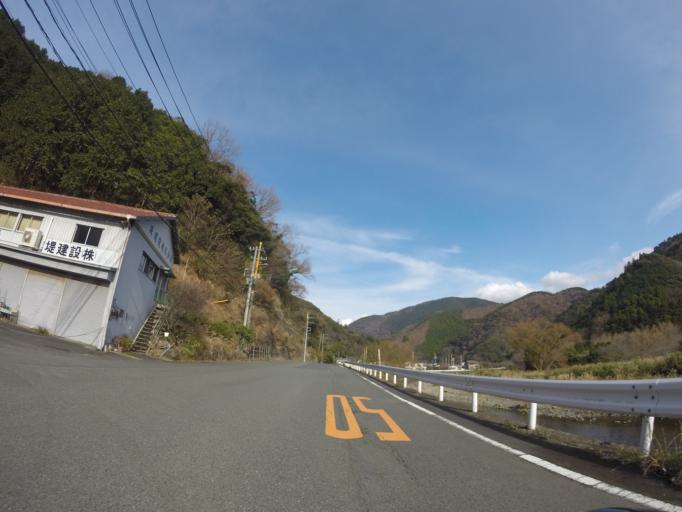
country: JP
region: Shizuoka
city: Heda
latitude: 34.7844
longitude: 138.7973
